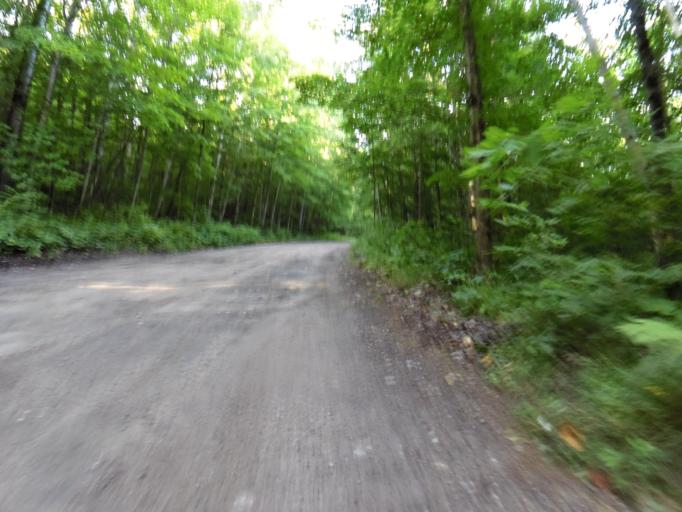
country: CA
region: Quebec
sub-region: Outaouais
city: Maniwaki
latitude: 46.3161
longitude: -76.0075
